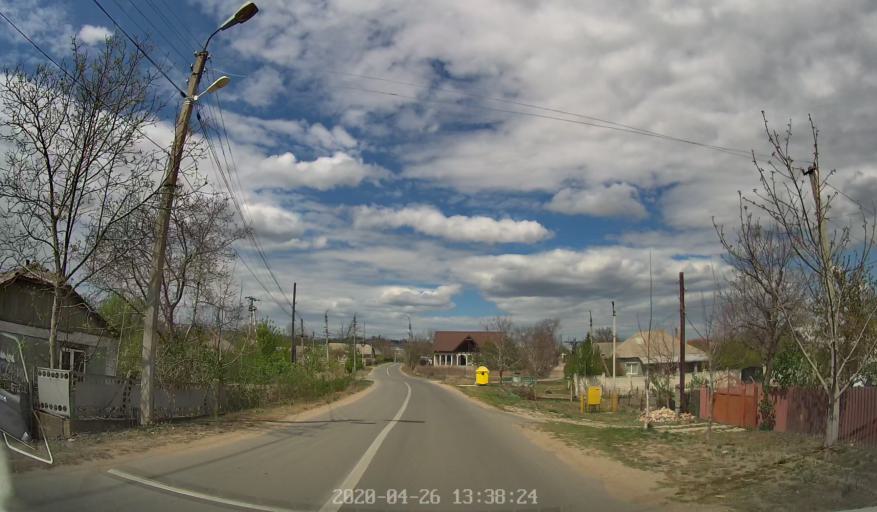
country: MD
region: Criuleni
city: Criuleni
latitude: 47.2078
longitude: 29.1670
